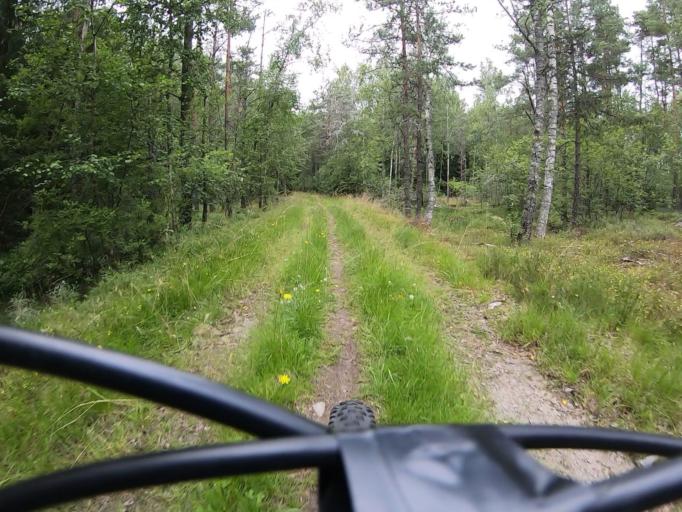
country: FI
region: Varsinais-Suomi
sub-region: Vakka-Suomi
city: Uusikaupunki
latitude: 60.8321
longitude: 21.4152
